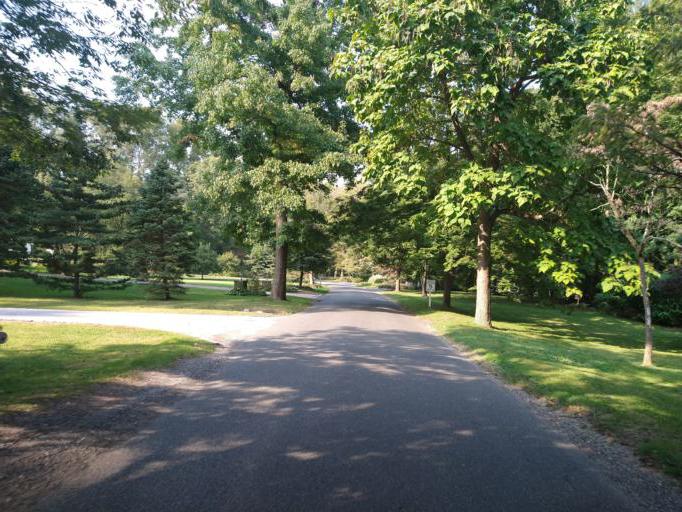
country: US
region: New York
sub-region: Nassau County
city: Lattingtown
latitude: 40.8924
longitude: -73.6005
